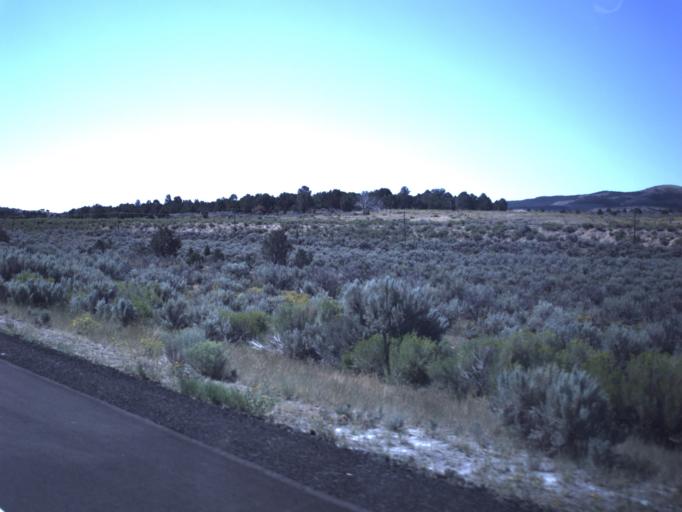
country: US
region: Utah
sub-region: Utah County
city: Genola
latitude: 39.9758
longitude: -112.2592
